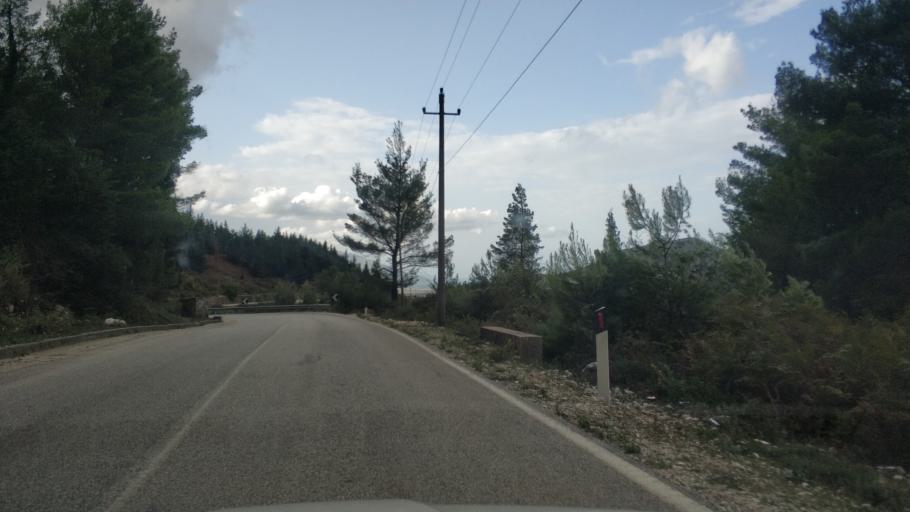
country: AL
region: Vlore
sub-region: Rrethi i Vlores
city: Orikum
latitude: 40.2593
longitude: 19.5260
